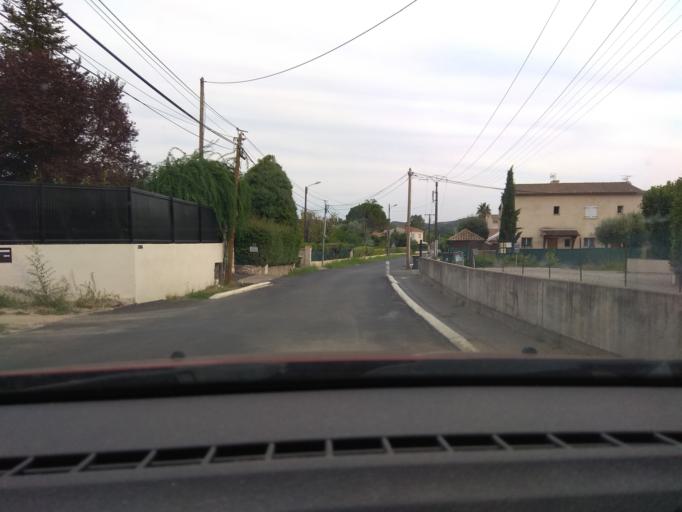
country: FR
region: Provence-Alpes-Cote d'Azur
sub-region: Departement des Alpes-Maritimes
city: La Colle-sur-Loup
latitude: 43.6767
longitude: 7.1089
